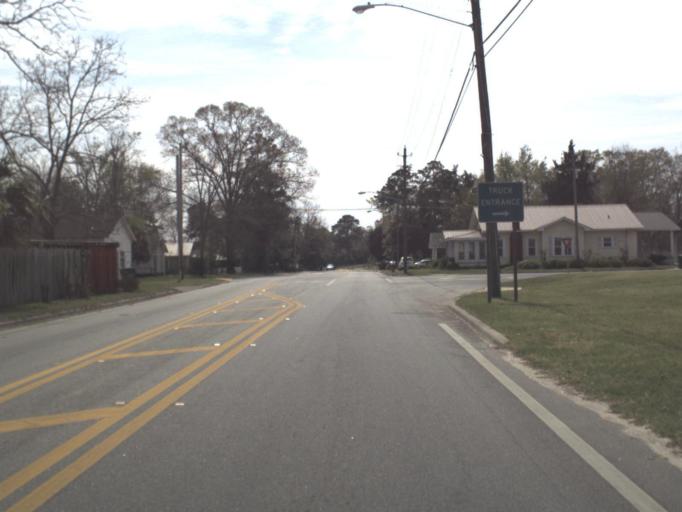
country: US
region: Florida
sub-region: Jackson County
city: Graceville
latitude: 30.9543
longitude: -85.5167
